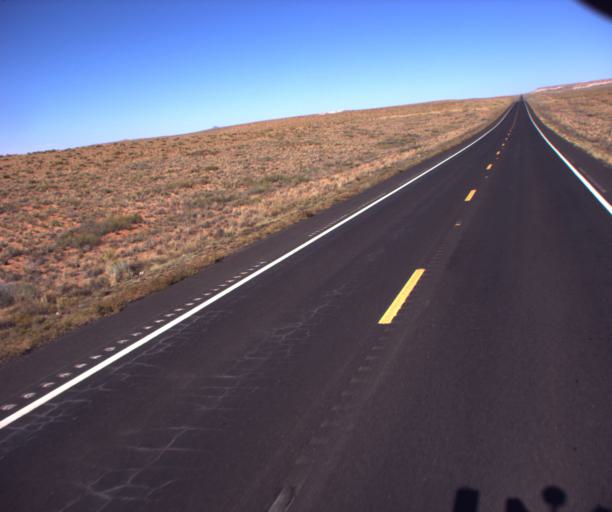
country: US
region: Arizona
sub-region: Coconino County
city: Tuba City
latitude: 36.1854
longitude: -111.0721
